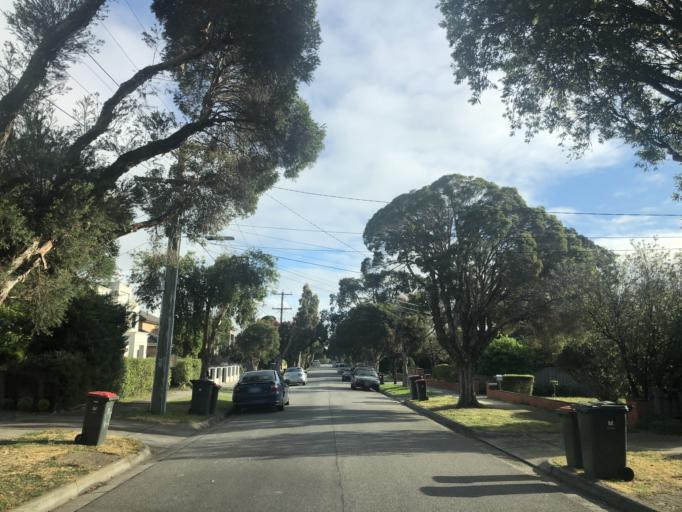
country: AU
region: Victoria
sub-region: Monash
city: Chadstone
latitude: -37.8877
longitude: 145.1191
